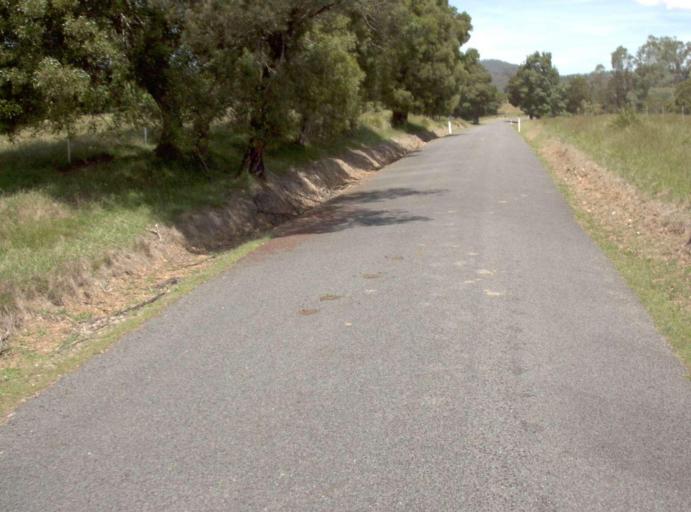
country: AU
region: New South Wales
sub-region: Bombala
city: Bombala
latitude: -37.4136
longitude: 149.0097
